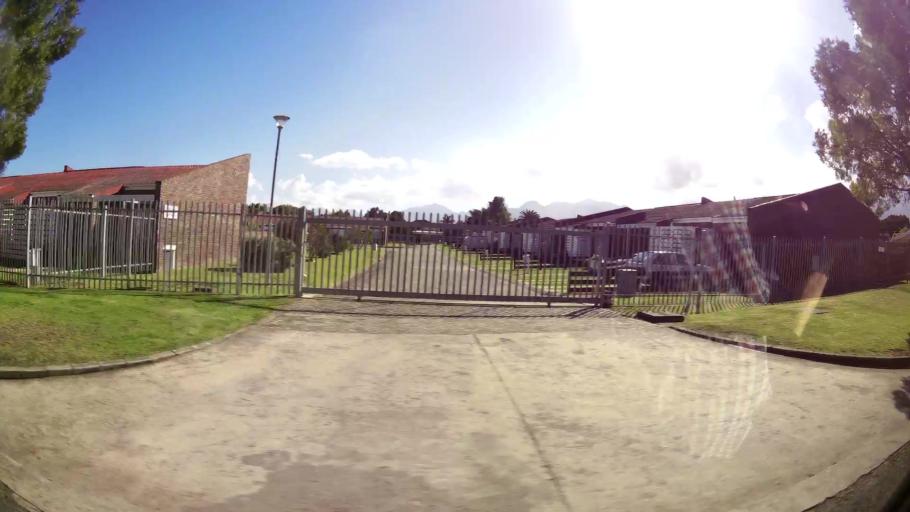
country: ZA
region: Western Cape
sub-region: Eden District Municipality
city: George
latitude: -33.9733
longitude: 22.4527
